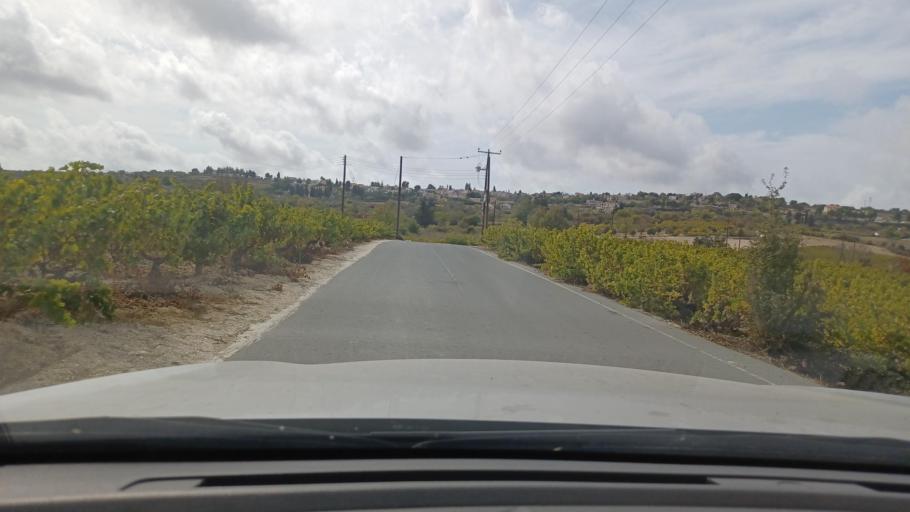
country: CY
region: Pafos
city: Pegeia
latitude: 34.9183
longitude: 32.4332
